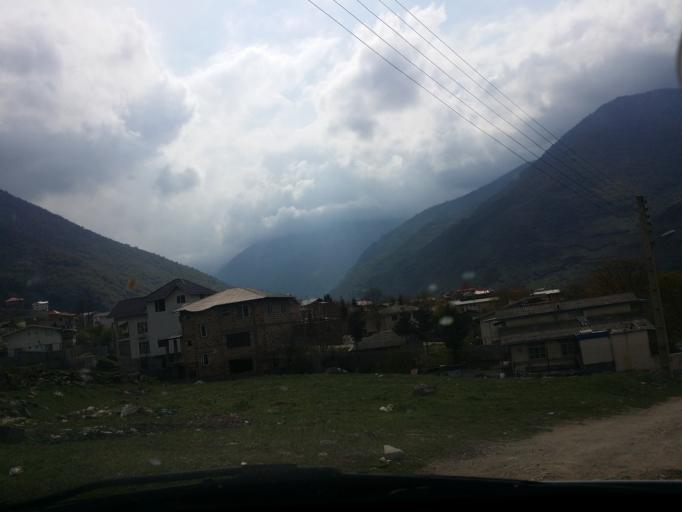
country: IR
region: Mazandaran
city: `Abbasabad
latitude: 36.4850
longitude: 51.1403
